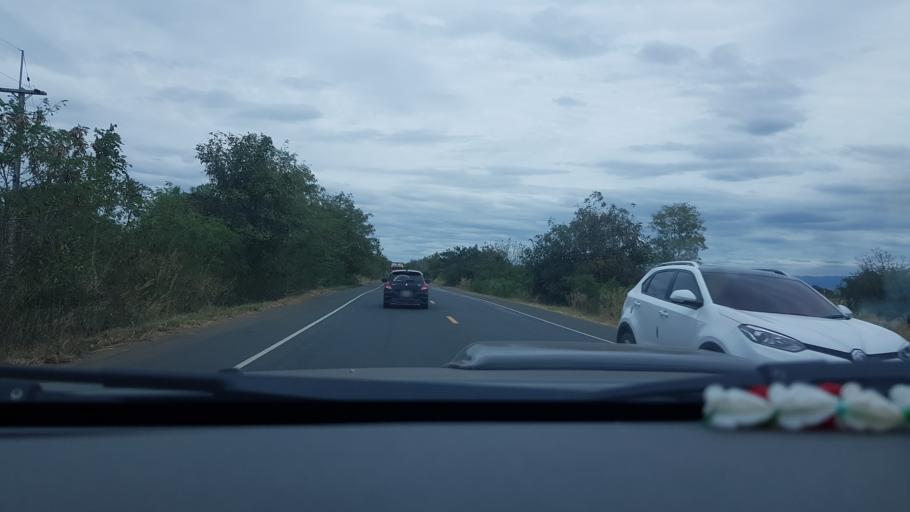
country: TH
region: Phetchabun
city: Phetchabun
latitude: 16.4676
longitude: 101.1255
